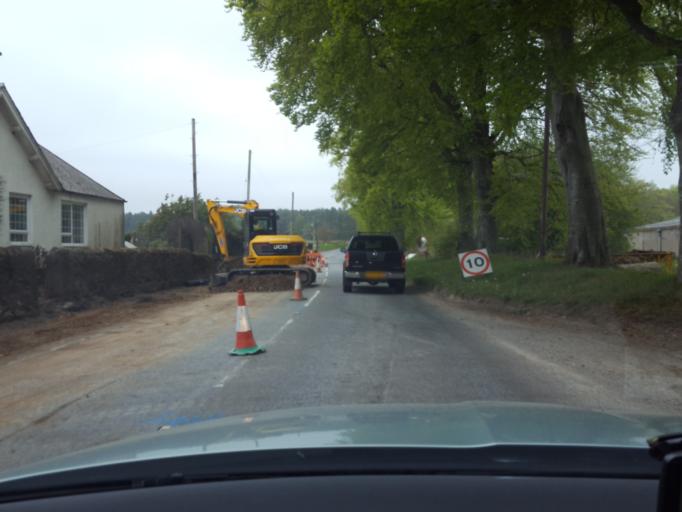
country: GB
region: Scotland
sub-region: Angus
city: Brechin
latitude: 56.7882
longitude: -2.6473
